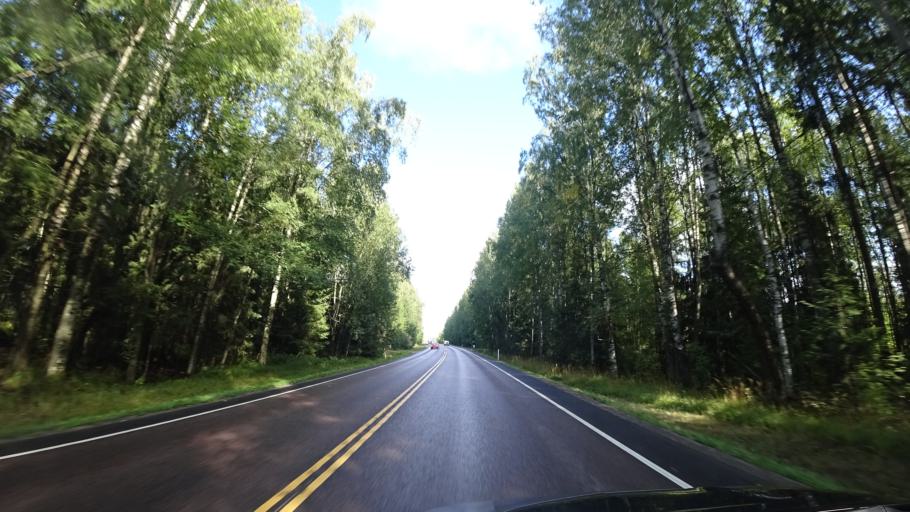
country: FI
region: Uusimaa
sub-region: Helsinki
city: Tuusula
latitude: 60.4947
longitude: 24.9383
